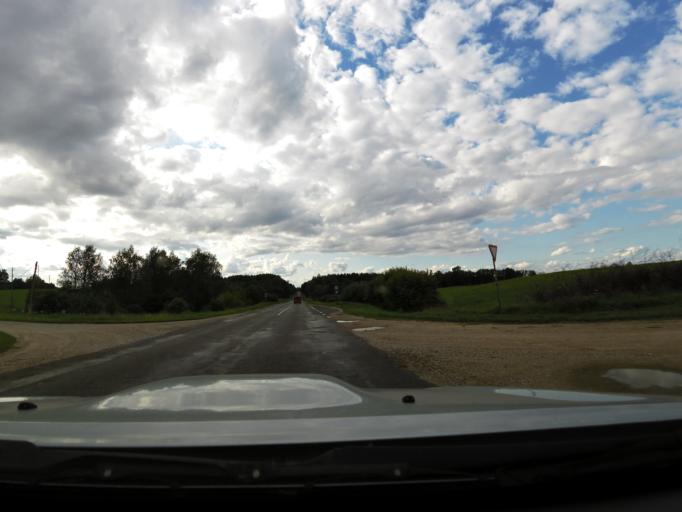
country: LV
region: Akniste
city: Akniste
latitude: 56.0024
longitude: 25.9529
